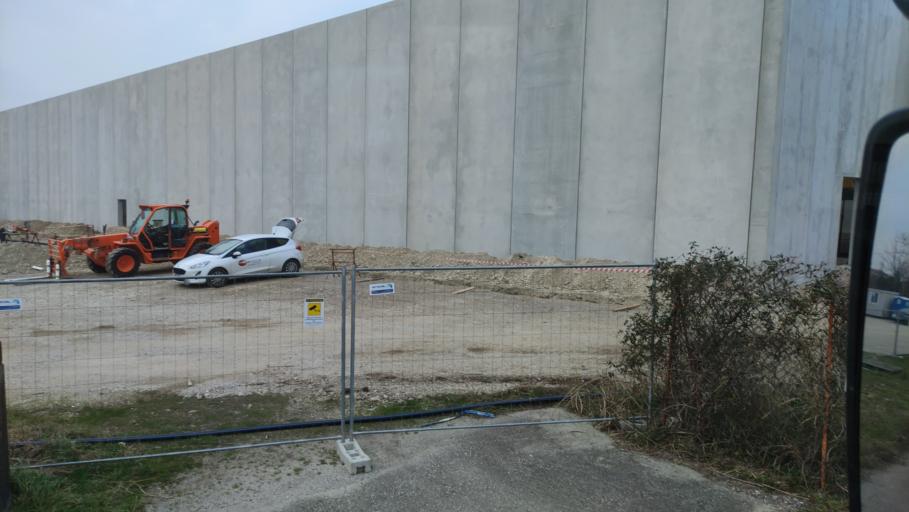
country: IT
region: Friuli Venezia Giulia
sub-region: Provincia di Gorizia
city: Villesse
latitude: 45.8697
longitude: 13.4467
